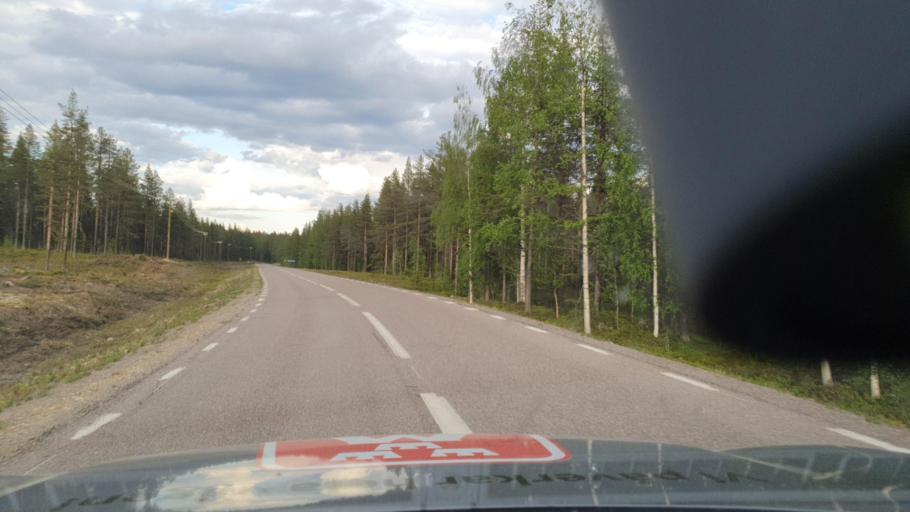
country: SE
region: Norrbotten
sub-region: Gallivare Kommun
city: Gaellivare
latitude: 66.9334
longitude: 21.2578
